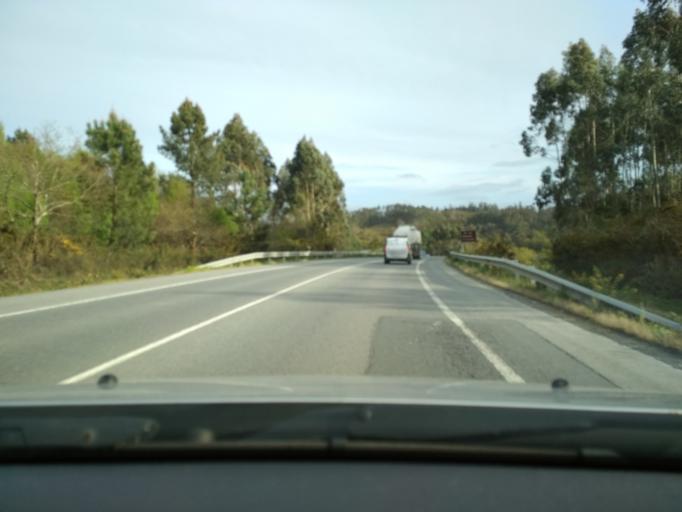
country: ES
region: Galicia
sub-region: Provincia da Coruna
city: Cerceda
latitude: 43.2223
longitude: -8.4586
